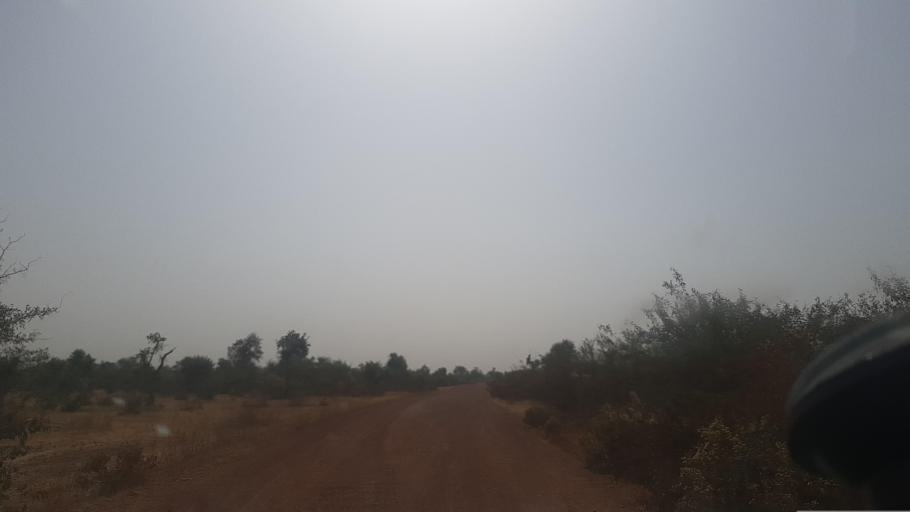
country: ML
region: Segou
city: Baroueli
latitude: 13.0625
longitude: -6.4740
